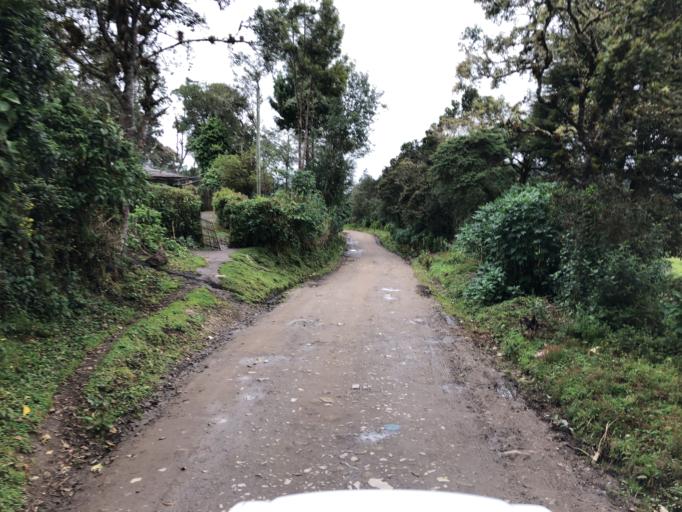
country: CO
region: Cauca
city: Totoro
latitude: 2.4926
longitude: -76.3453
